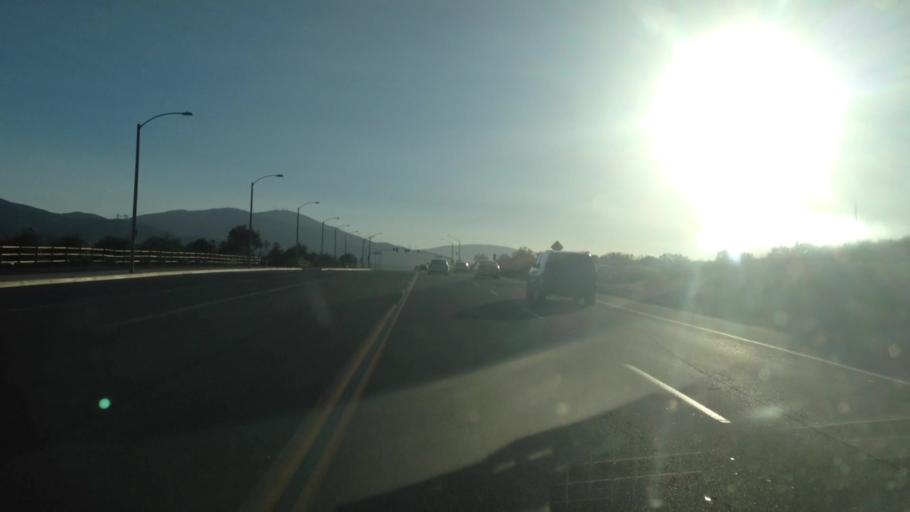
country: US
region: California
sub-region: Los Angeles County
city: Palmdale
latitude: 34.5580
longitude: -118.1223
